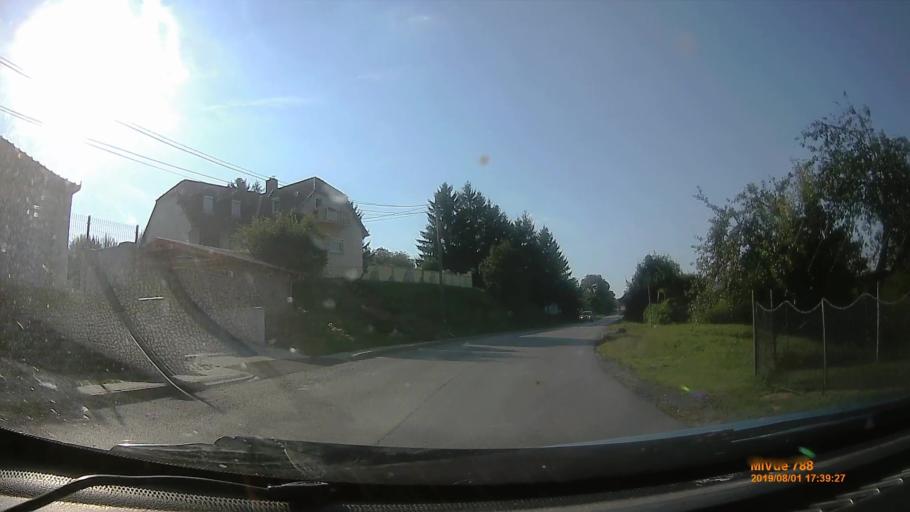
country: HU
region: Baranya
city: Komlo
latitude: 46.1972
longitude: 18.1921
